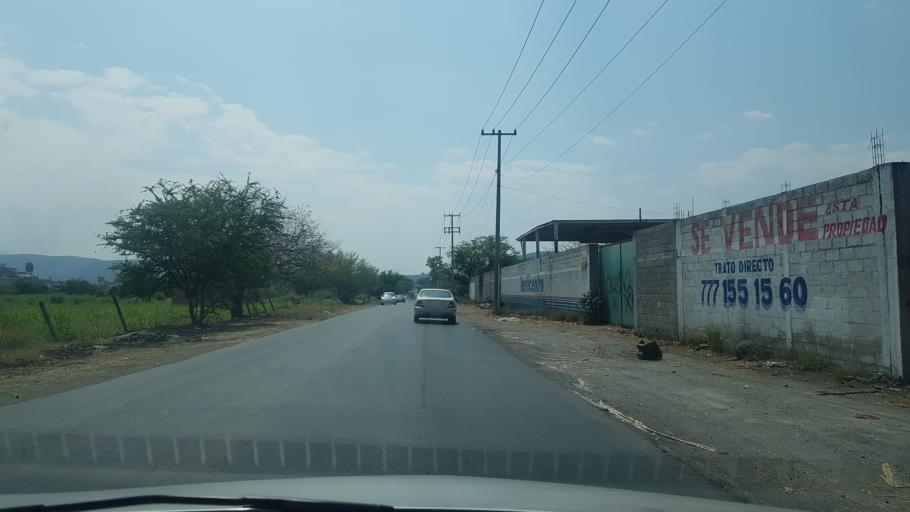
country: MX
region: Morelos
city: Zacatepec
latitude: 18.6589
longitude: -99.1803
